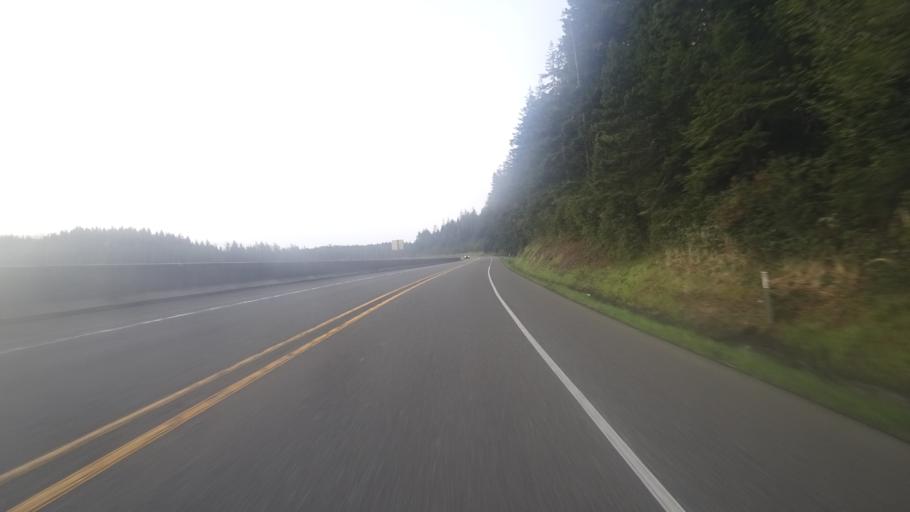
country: US
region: Oregon
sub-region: Coos County
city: Lakeside
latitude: 43.6383
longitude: -124.1888
